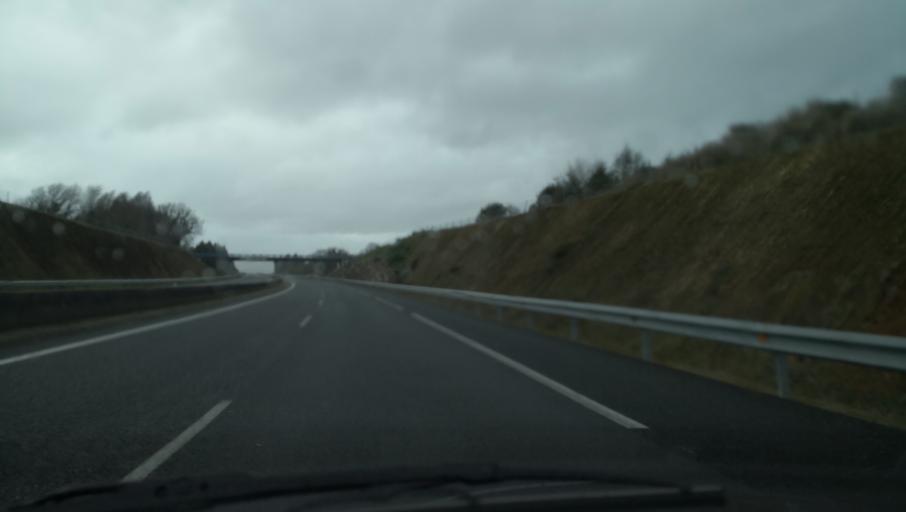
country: ES
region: Galicia
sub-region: Provincia de Pontevedra
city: Silleda
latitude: 42.6897
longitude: -8.1786
